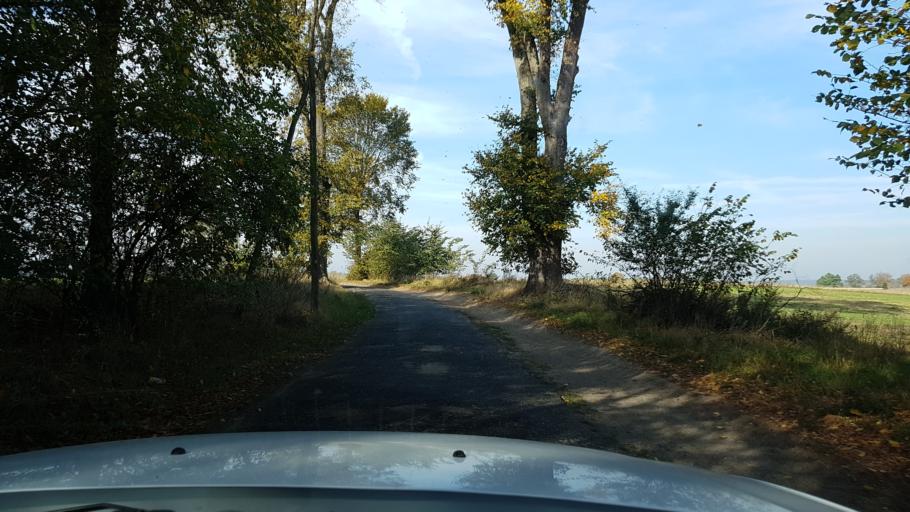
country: PL
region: West Pomeranian Voivodeship
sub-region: Powiat mysliborski
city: Mysliborz
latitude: 52.9350
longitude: 14.9353
